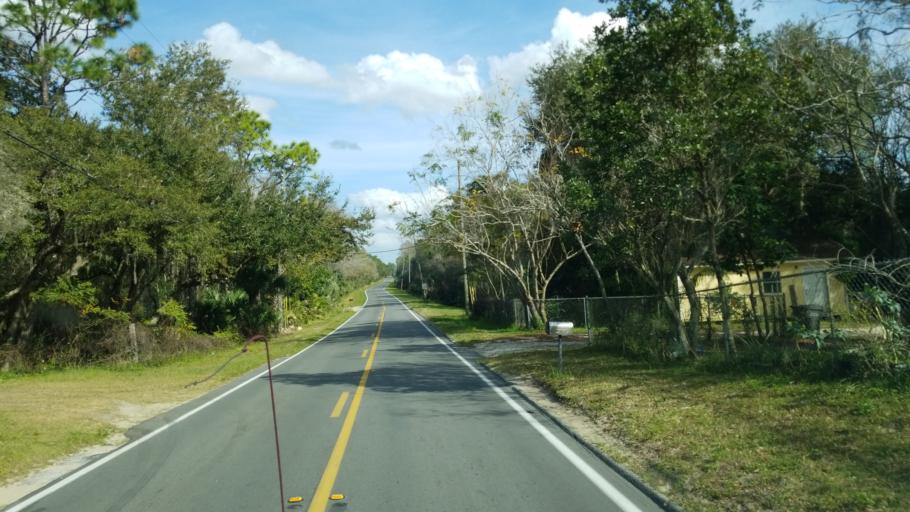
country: US
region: Florida
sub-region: Polk County
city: Davenport
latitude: 28.1467
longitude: -81.5750
